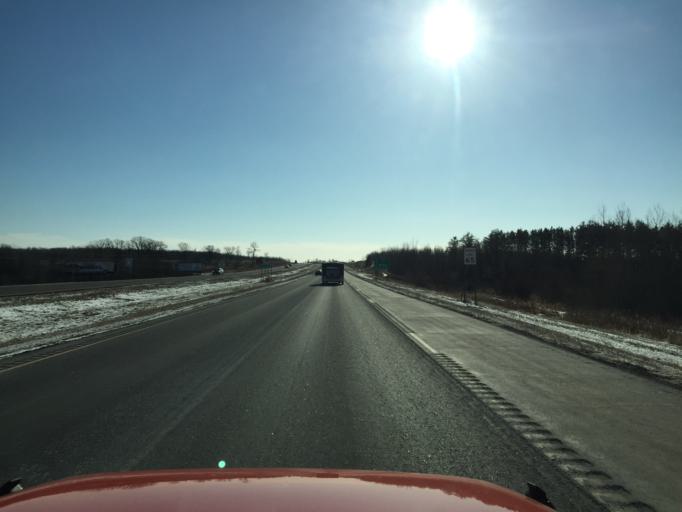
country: US
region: Minnesota
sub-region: Mille Lacs County
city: Milaca
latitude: 45.7776
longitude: -93.6483
